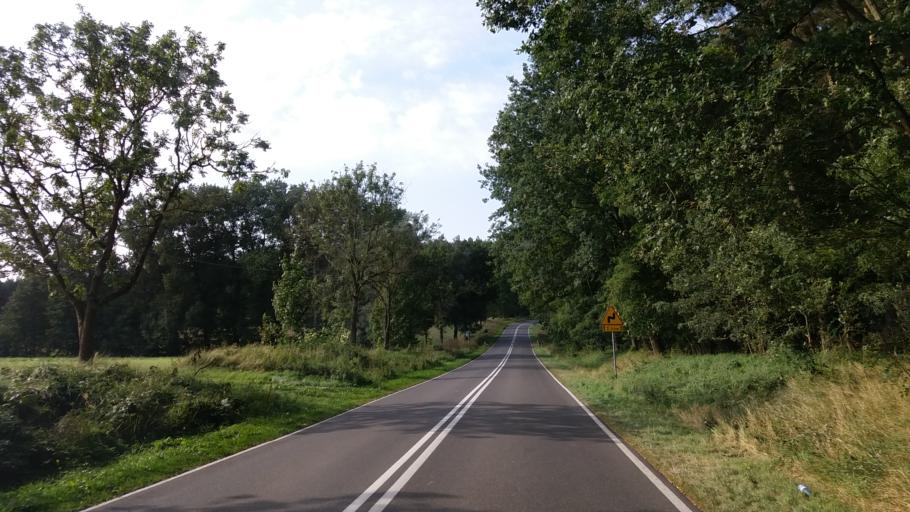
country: PL
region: West Pomeranian Voivodeship
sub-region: Powiat stargardzki
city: Suchan
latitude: 53.2429
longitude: 15.3223
